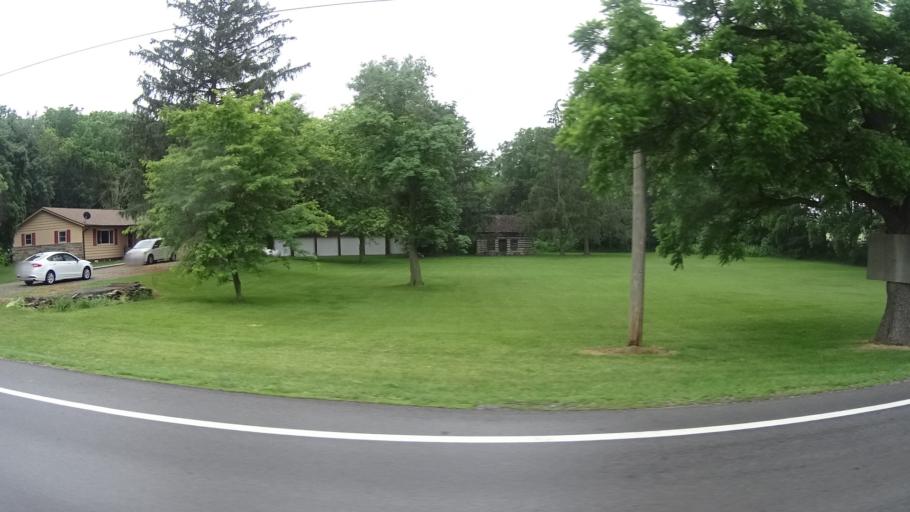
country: US
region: Ohio
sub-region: Huron County
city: Bellevue
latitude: 41.3442
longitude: -82.8304
